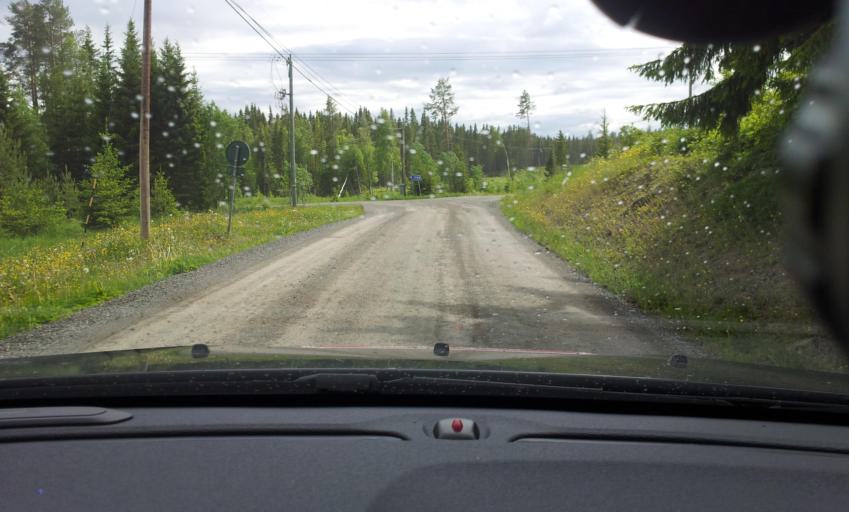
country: SE
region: Jaemtland
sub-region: OEstersunds Kommun
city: Brunflo
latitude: 63.0183
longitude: 14.7706
